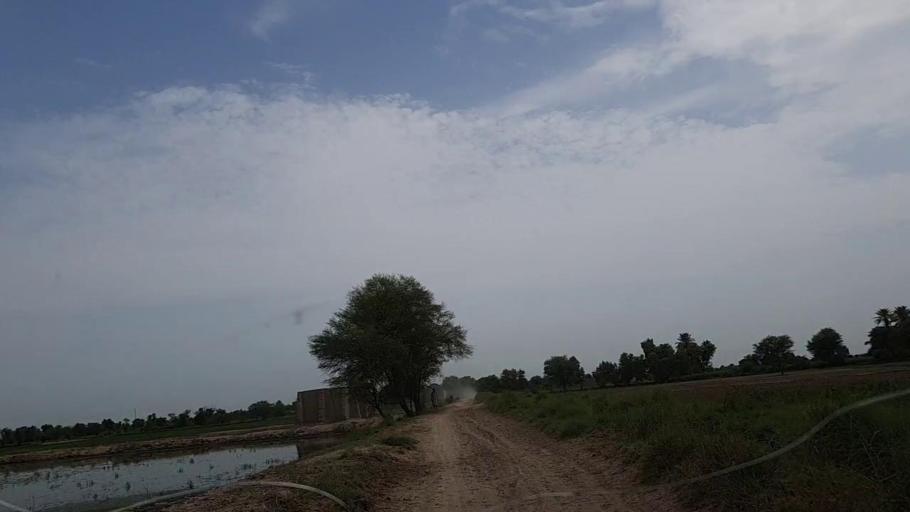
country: PK
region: Sindh
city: Tharu Shah
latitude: 26.9004
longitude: 68.0695
